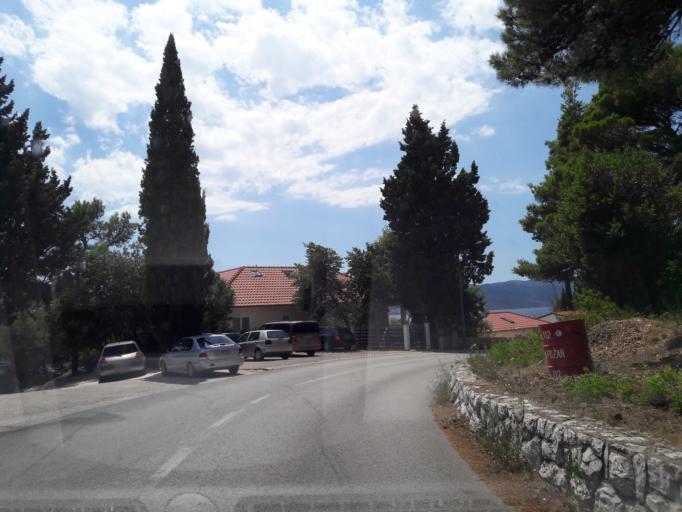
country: HR
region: Dubrovacko-Neretvanska
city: Orebic
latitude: 42.9749
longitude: 17.1567
